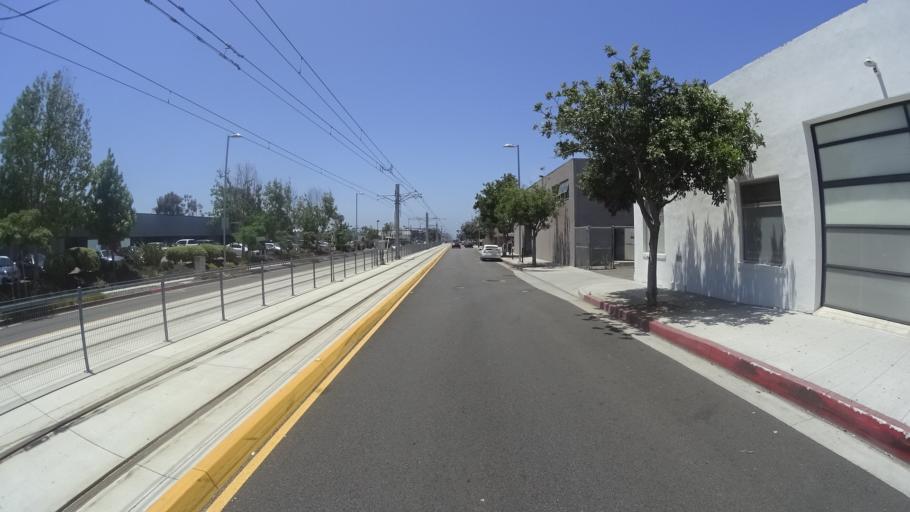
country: US
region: California
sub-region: Los Angeles County
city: Santa Monica
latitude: 34.0182
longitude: -118.4867
